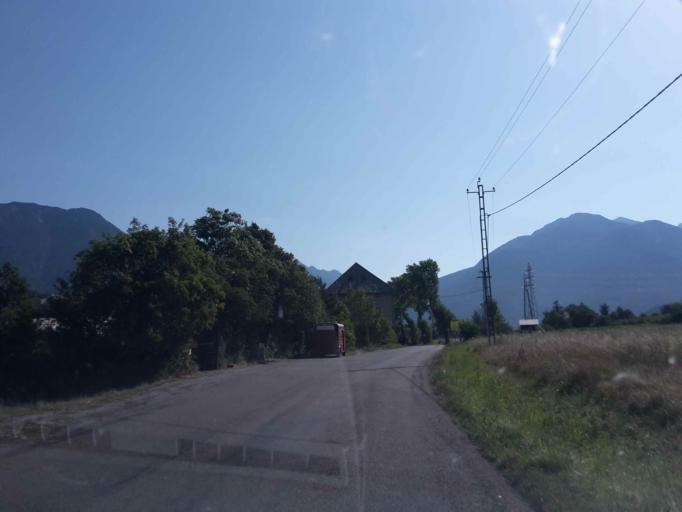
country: FR
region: Provence-Alpes-Cote d'Azur
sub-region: Departement des Hautes-Alpes
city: Guillestre
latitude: 44.6605
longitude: 6.6101
